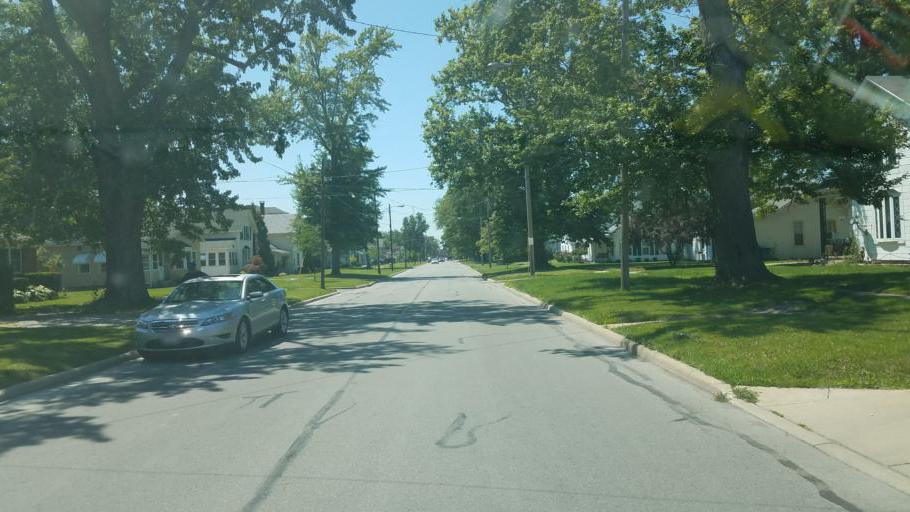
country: US
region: Ohio
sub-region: Ottawa County
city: Port Clinton
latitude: 41.5106
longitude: -82.9306
